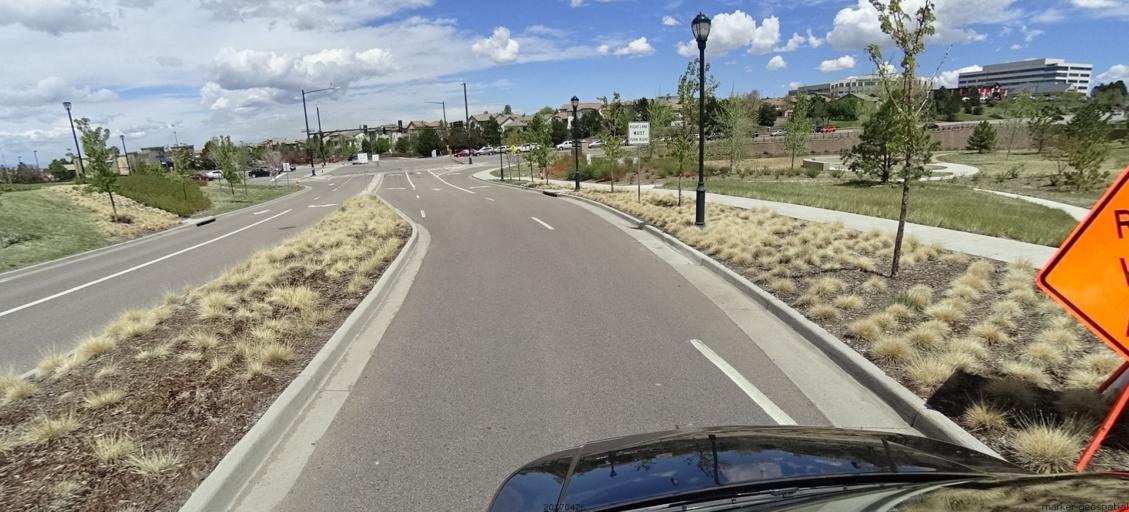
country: US
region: Colorado
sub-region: Adams County
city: Lone Tree
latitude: 39.5353
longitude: -104.8771
